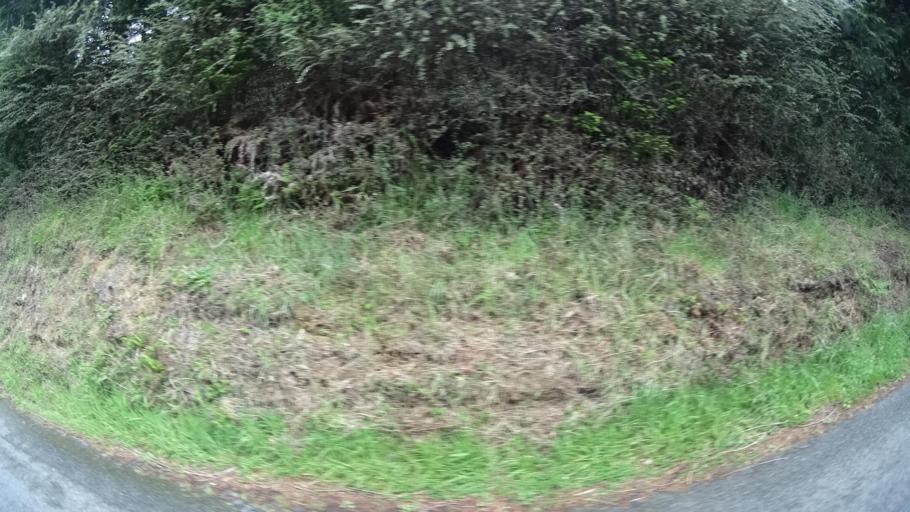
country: US
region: California
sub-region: Humboldt County
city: Bayside
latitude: 40.8401
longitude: -124.0244
